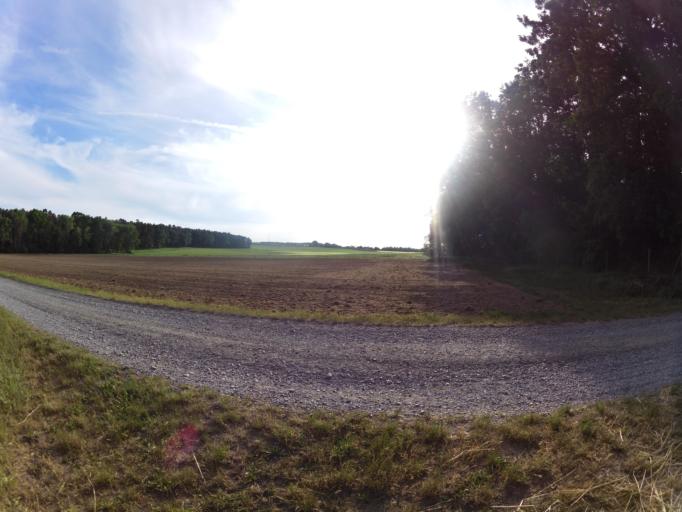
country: DE
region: Bavaria
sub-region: Regierungsbezirk Unterfranken
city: Sommerhausen
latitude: 49.6983
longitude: 10.0561
